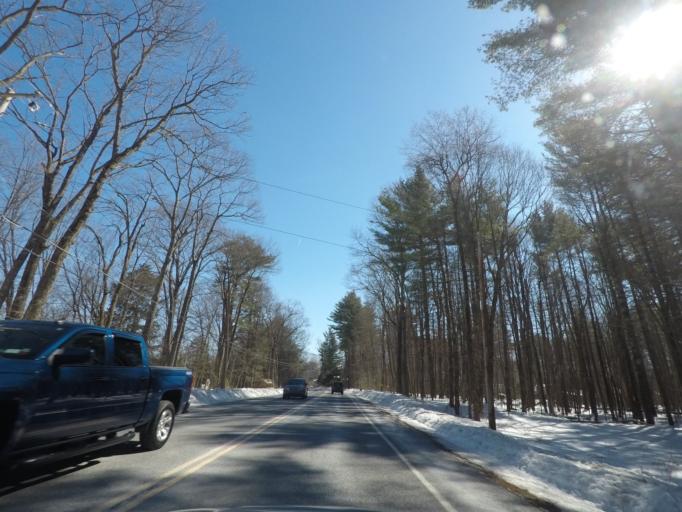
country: US
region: New York
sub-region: Saratoga County
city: Saratoga Springs
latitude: 43.0512
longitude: -73.7454
